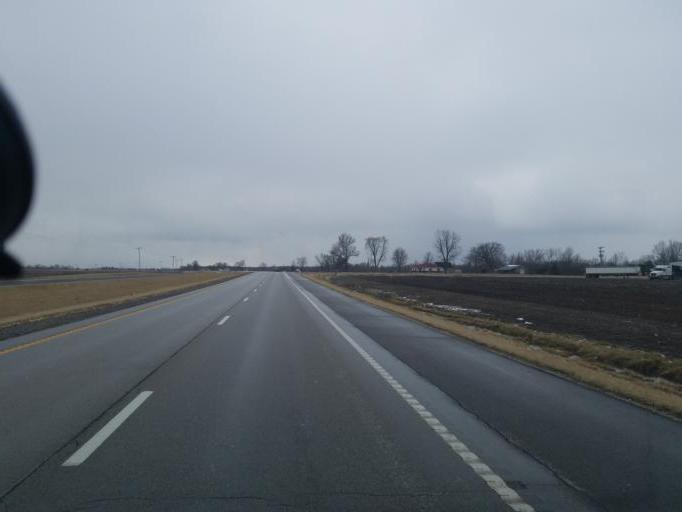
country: US
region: Missouri
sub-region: Macon County
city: Macon
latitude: 39.8490
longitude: -92.4804
